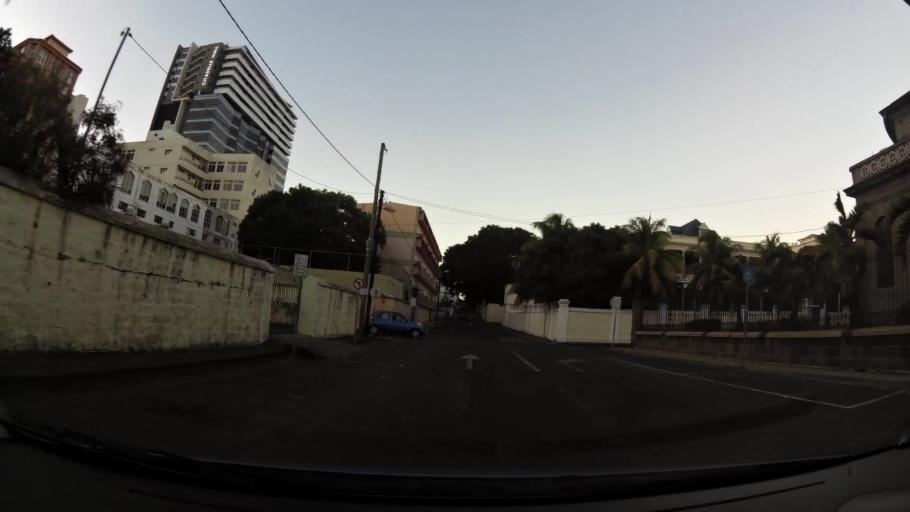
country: MU
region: Port Louis
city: Port Louis
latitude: -20.1642
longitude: 57.5064
